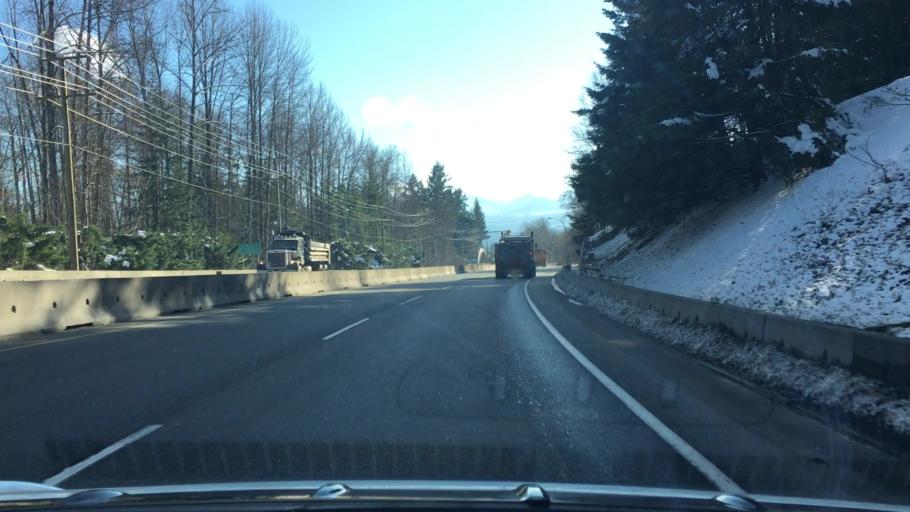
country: CA
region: British Columbia
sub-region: Cowichan Valley Regional District
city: Ladysmith
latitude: 49.0645
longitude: -123.8770
